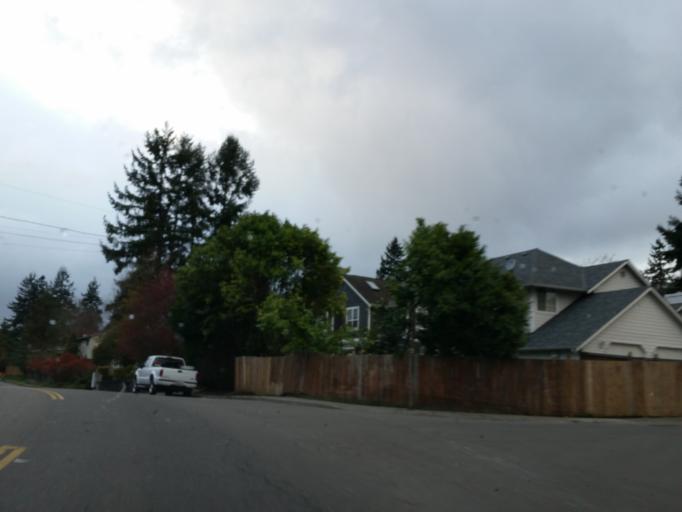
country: US
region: Washington
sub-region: Snohomish County
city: Alderwood Manor
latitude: 47.8101
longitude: -122.2726
